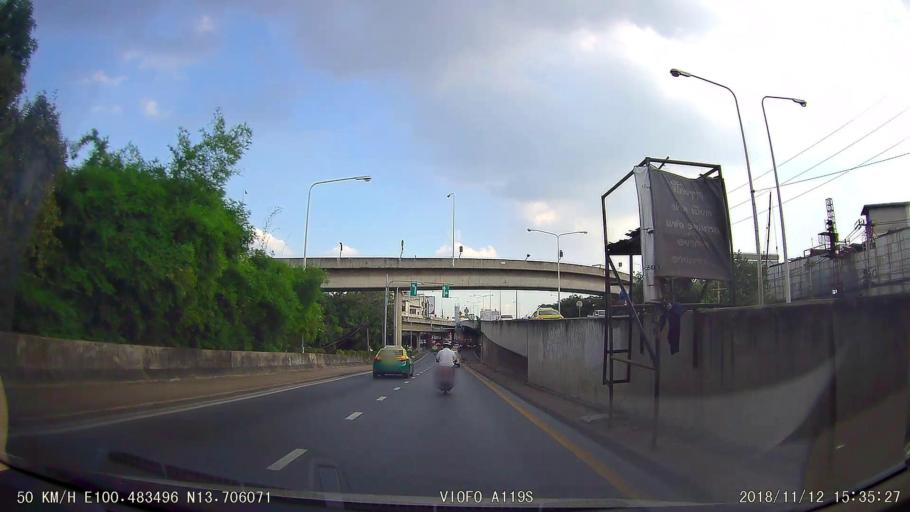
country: TH
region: Bangkok
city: Bangkok Yai
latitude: 13.7060
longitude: 100.4836
